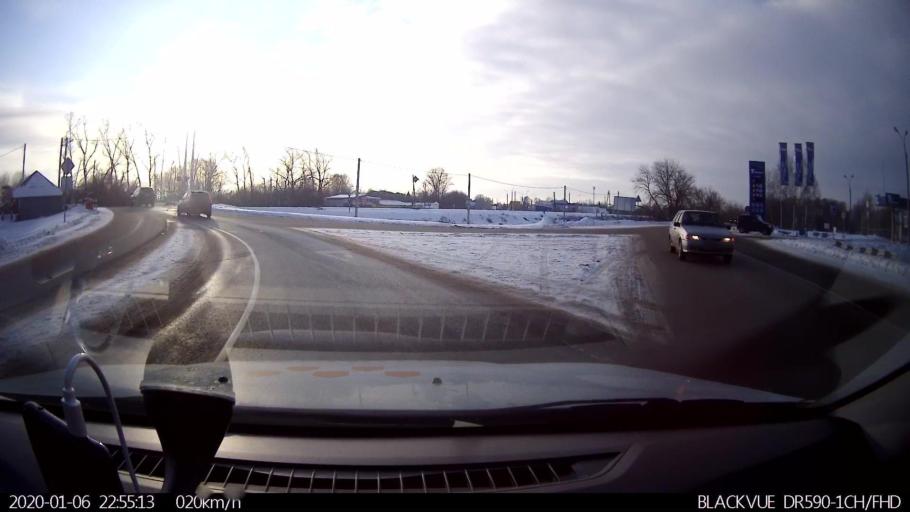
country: RU
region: Nizjnij Novgorod
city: Bogorodsk
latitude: 56.1167
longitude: 43.5410
